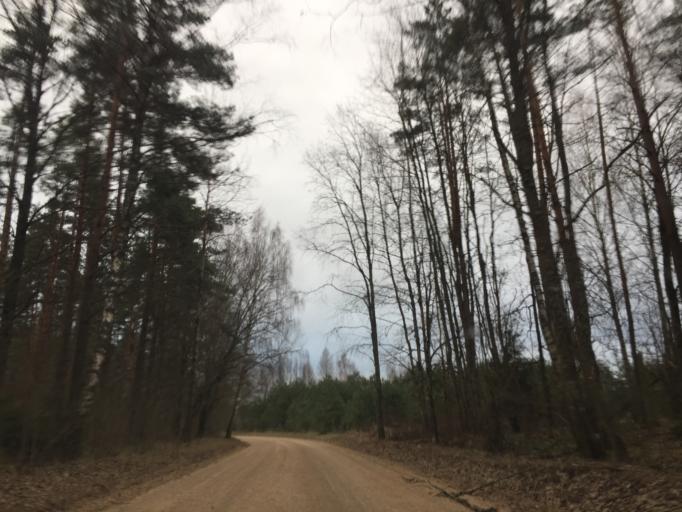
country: LV
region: Cesu Rajons
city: Cesis
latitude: 57.3481
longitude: 25.2582
